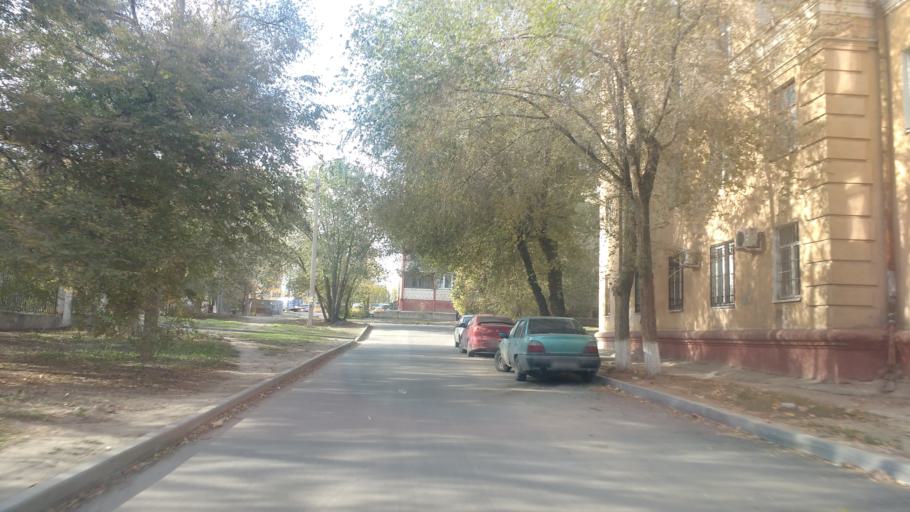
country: RU
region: Volgograd
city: Krasnoslobodsk
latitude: 48.7617
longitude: 44.5555
